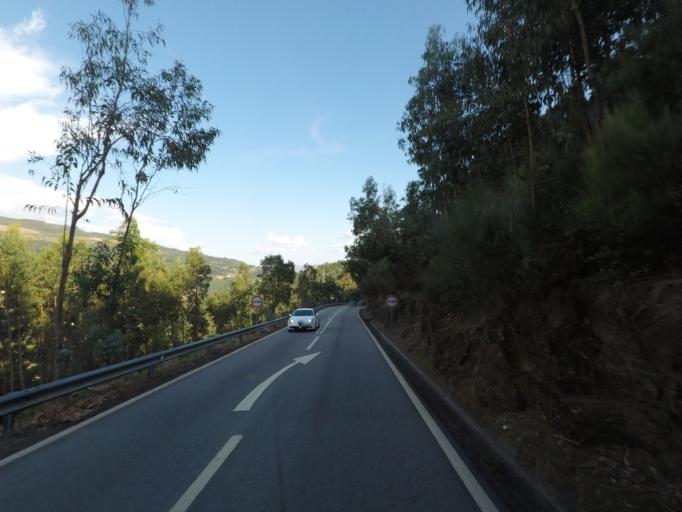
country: PT
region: Vila Real
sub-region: Mesao Frio
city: Mesao Frio
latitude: 41.1754
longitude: -7.9166
